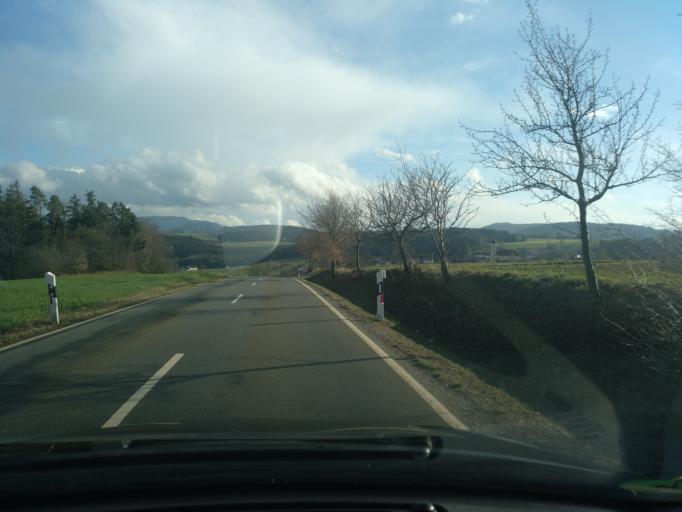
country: DE
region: Bavaria
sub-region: Upper Palatinate
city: Zandt
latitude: 49.1403
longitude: 12.7180
